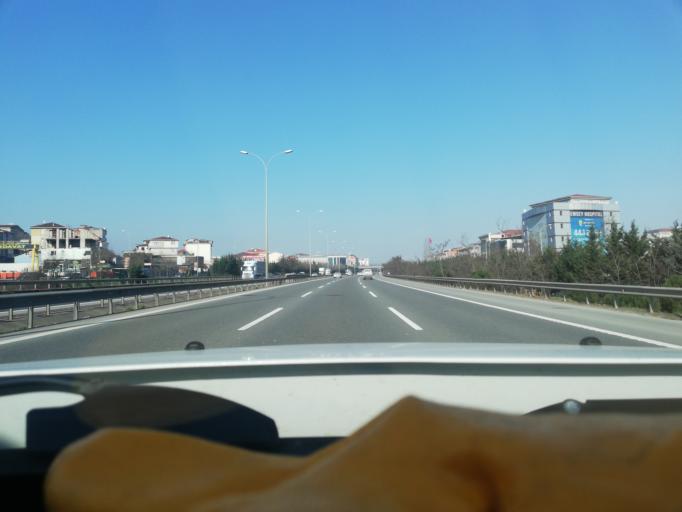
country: TR
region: Istanbul
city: Sultanbeyli
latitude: 40.9626
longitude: 29.2783
